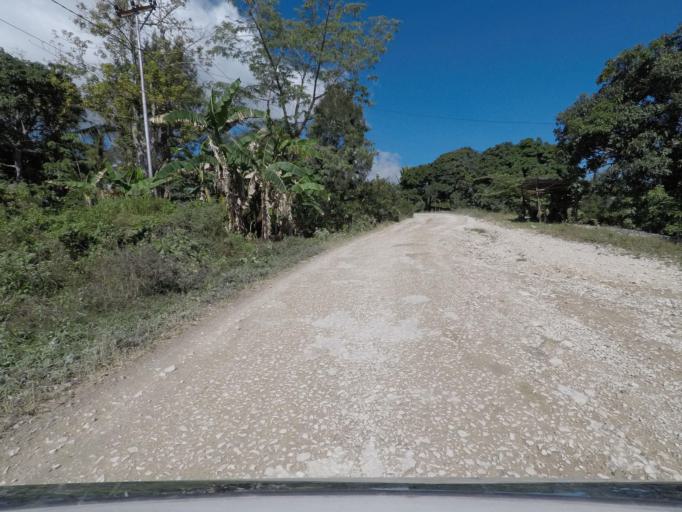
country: TL
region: Baucau
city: Venilale
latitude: -8.6729
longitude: 126.3660
